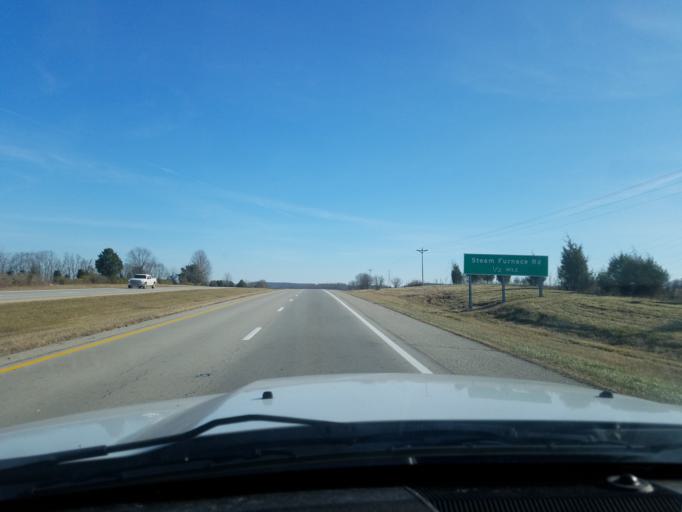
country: US
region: Ohio
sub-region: Adams County
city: Peebles
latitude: 38.9355
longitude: -83.4032
